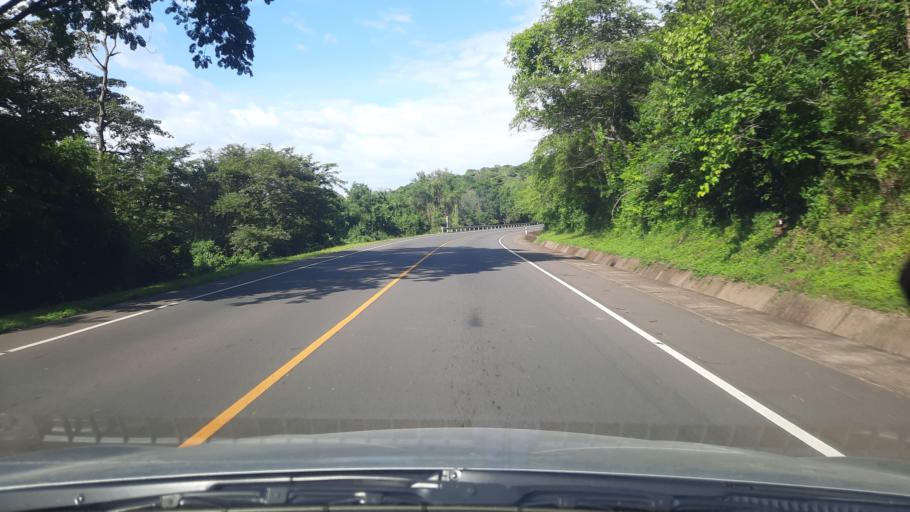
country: NI
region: Leon
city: Telica
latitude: 12.6903
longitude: -86.8548
